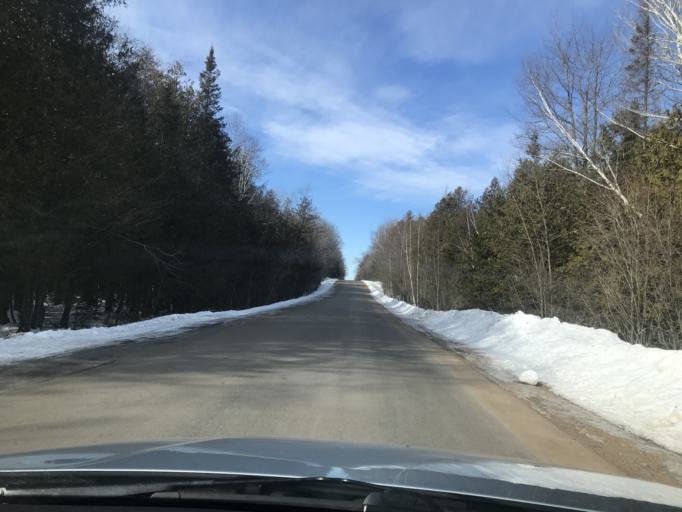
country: US
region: Wisconsin
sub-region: Oconto County
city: Gillett
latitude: 44.9616
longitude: -88.2753
